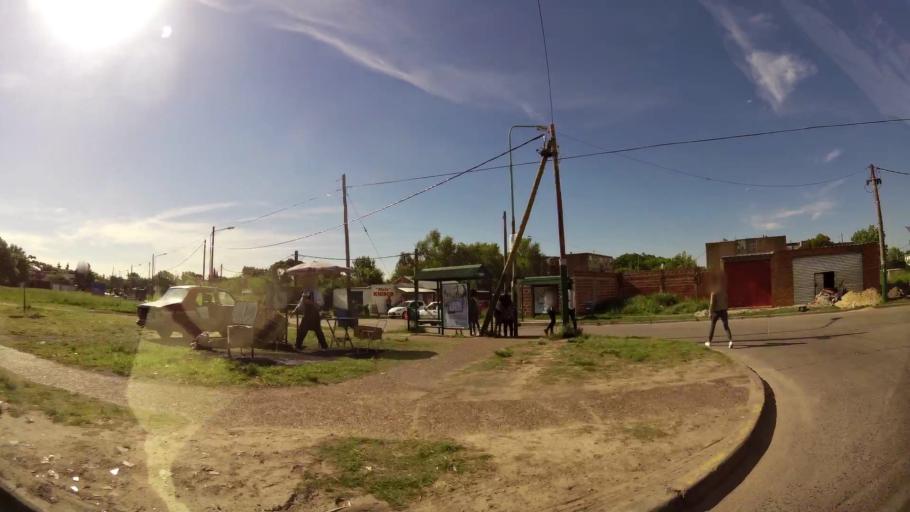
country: AR
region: Buenos Aires
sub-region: Partido de Almirante Brown
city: Adrogue
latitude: -34.8226
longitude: -58.3443
